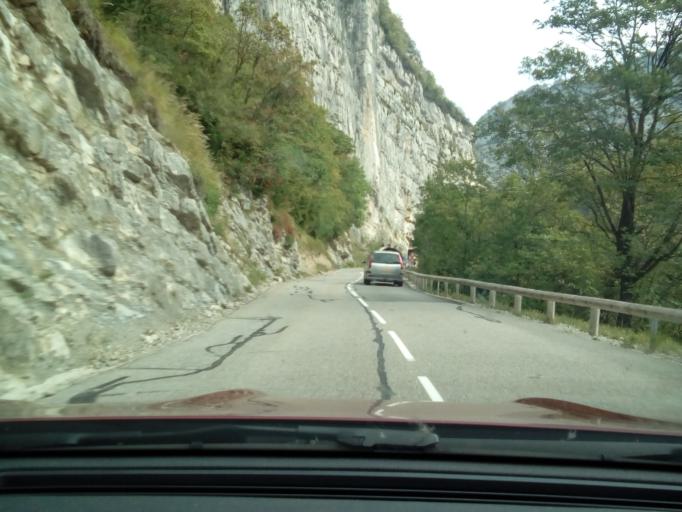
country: FR
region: Rhone-Alpes
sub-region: Departement de la Drome
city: Saint-Laurent-en-Royans
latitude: 45.0134
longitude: 5.4066
